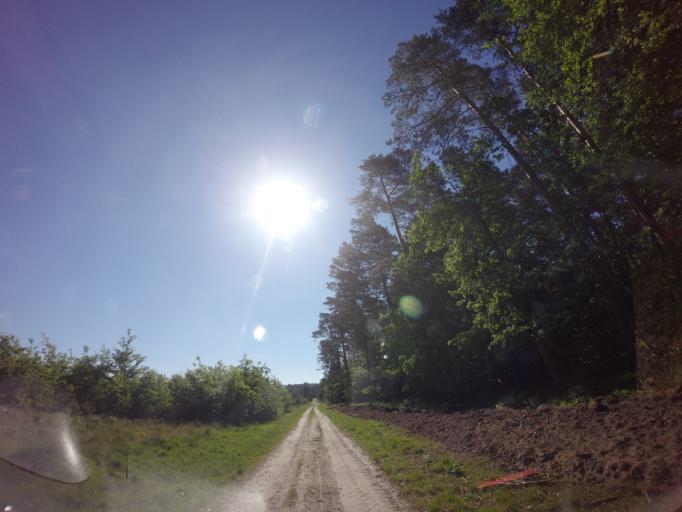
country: PL
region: West Pomeranian Voivodeship
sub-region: Powiat choszczenski
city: Drawno
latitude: 53.2345
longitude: 15.6859
